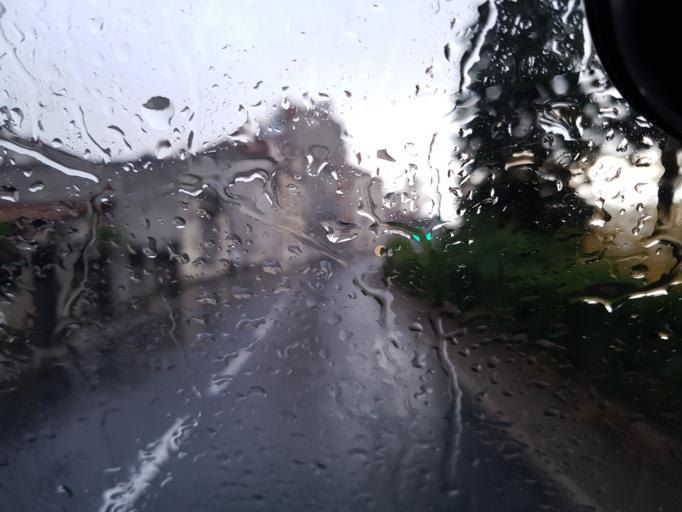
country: FR
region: Auvergne
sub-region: Departement de la Haute-Loire
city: Le Puy-en-Velay
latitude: 45.0421
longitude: 3.8926
